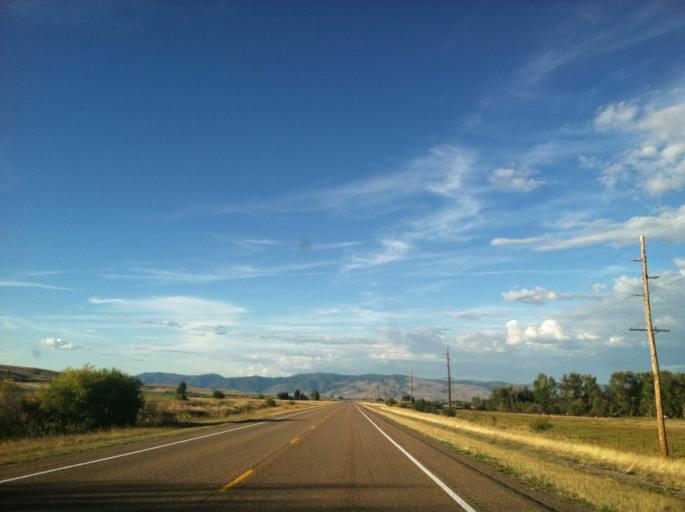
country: US
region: Montana
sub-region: Granite County
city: Philipsburg
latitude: 46.5446
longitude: -113.2196
